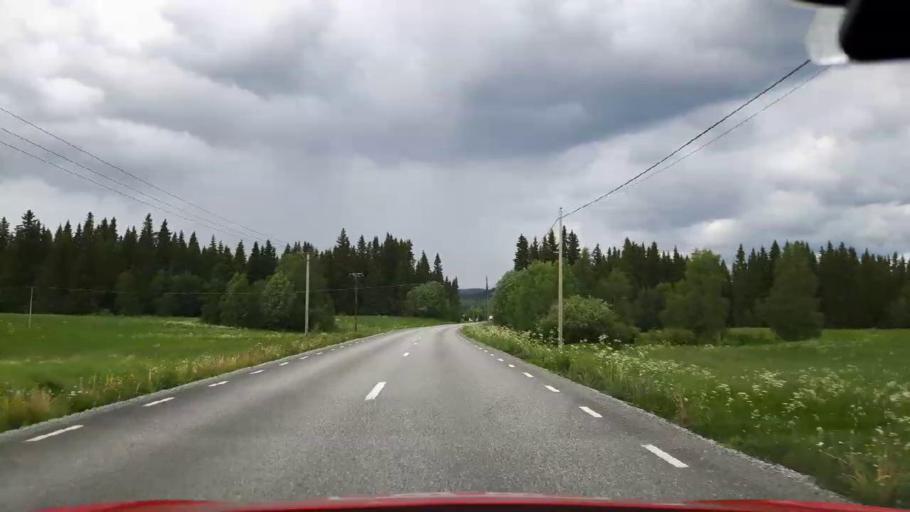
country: SE
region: Jaemtland
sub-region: Krokoms Kommun
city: Krokom
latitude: 63.6763
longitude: 14.3409
